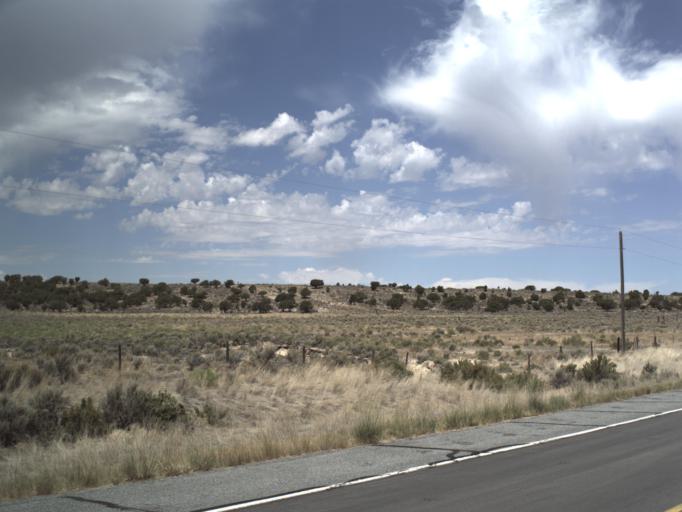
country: US
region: Utah
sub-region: Utah County
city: Eagle Mountain
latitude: 40.0456
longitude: -112.2930
